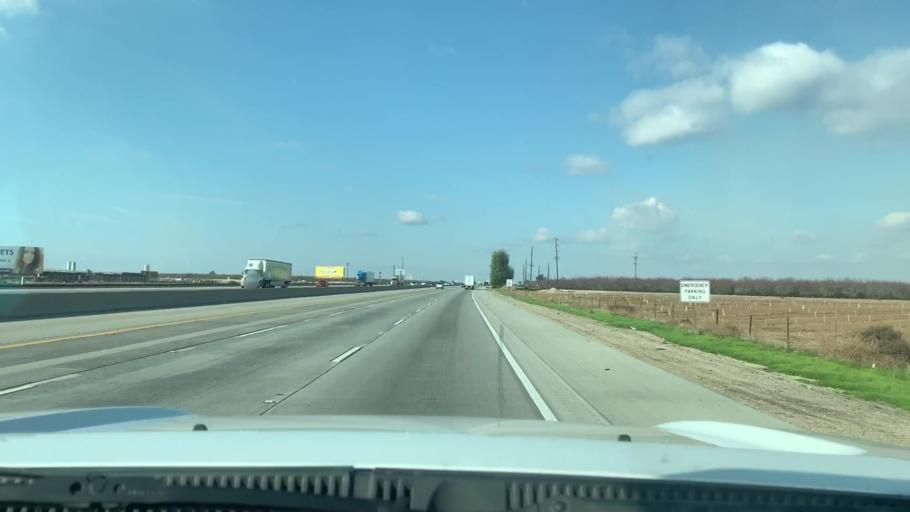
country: US
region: California
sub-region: Kern County
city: Shafter
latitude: 35.5042
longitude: -119.1701
